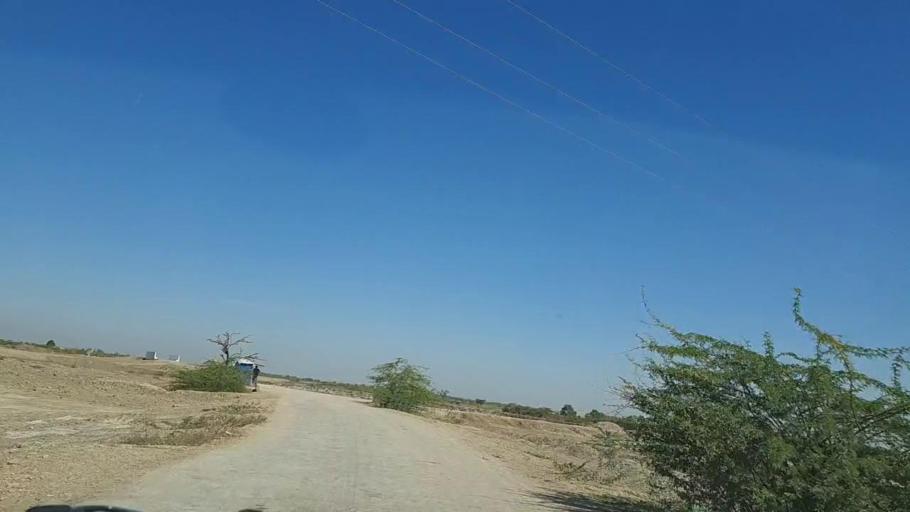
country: PK
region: Sindh
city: Dhoro Naro
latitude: 25.4741
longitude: 69.5268
